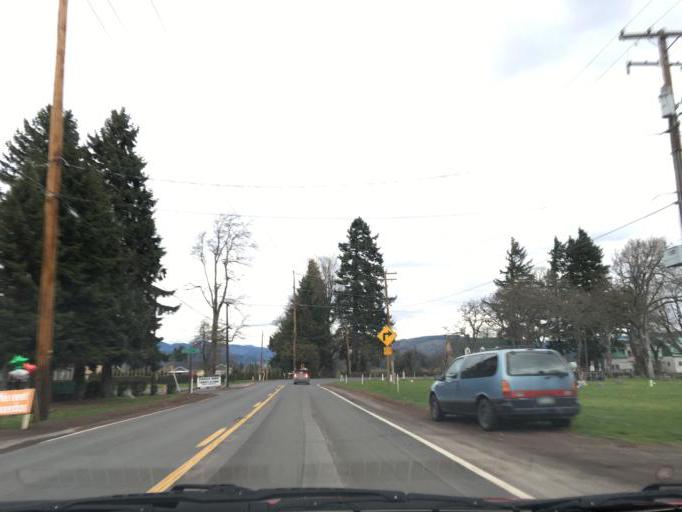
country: US
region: Oregon
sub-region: Hood River County
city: Hood River
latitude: 45.6847
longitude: -121.5289
